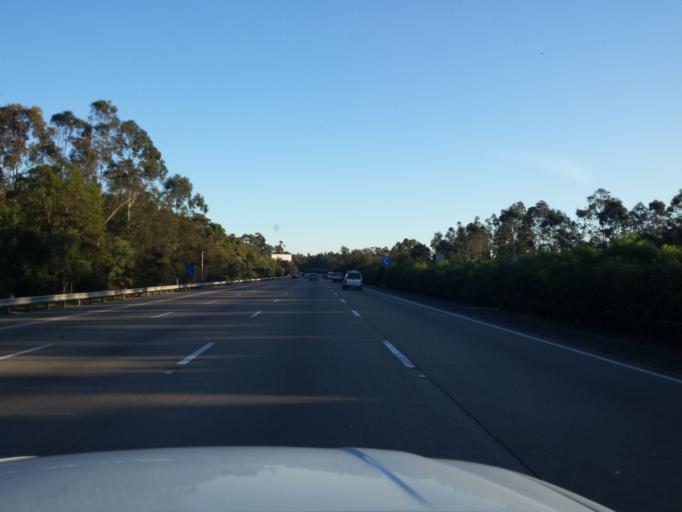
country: AU
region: Queensland
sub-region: Gold Coast
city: Oxenford
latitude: -27.8376
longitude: 153.3029
